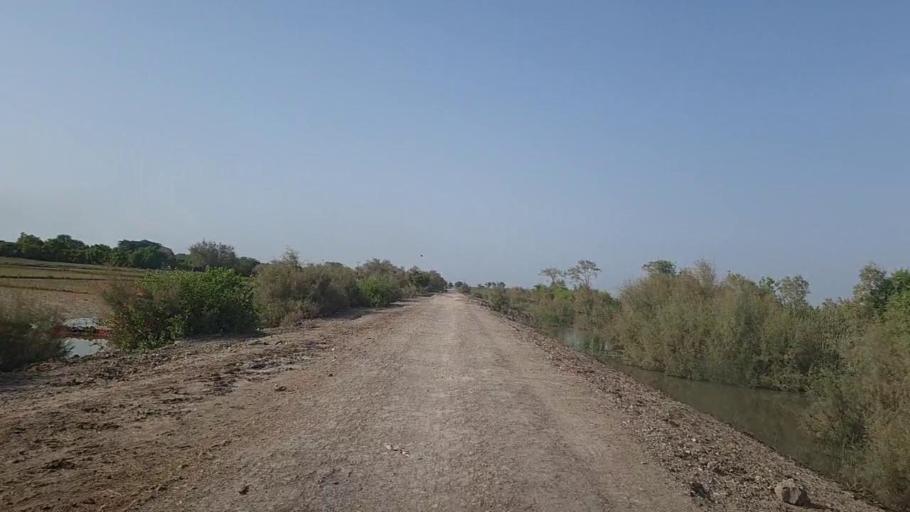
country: PK
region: Sindh
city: Sita Road
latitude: 27.0999
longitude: 67.8736
